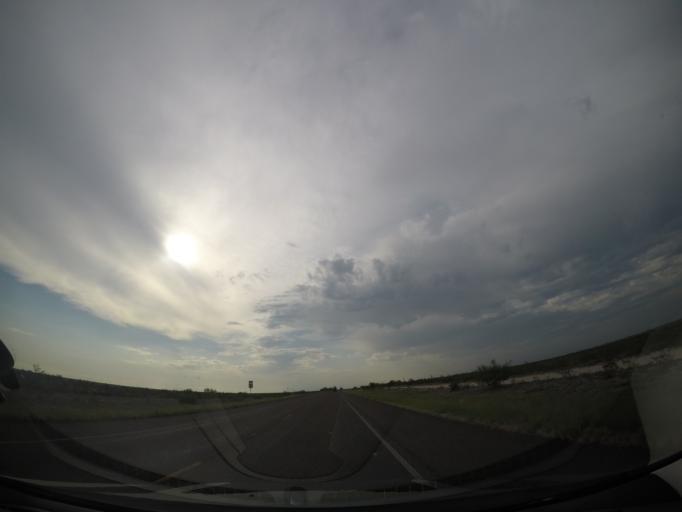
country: US
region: Texas
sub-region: Terrell County
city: Sanderson
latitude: 29.9337
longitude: -101.9379
